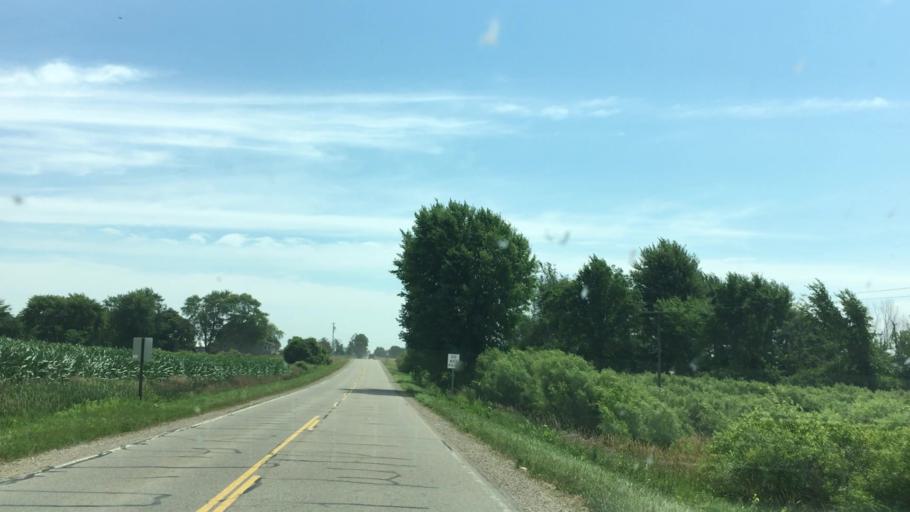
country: US
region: Michigan
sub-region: Sanilac County
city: Marlette
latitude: 43.2552
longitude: -83.0712
